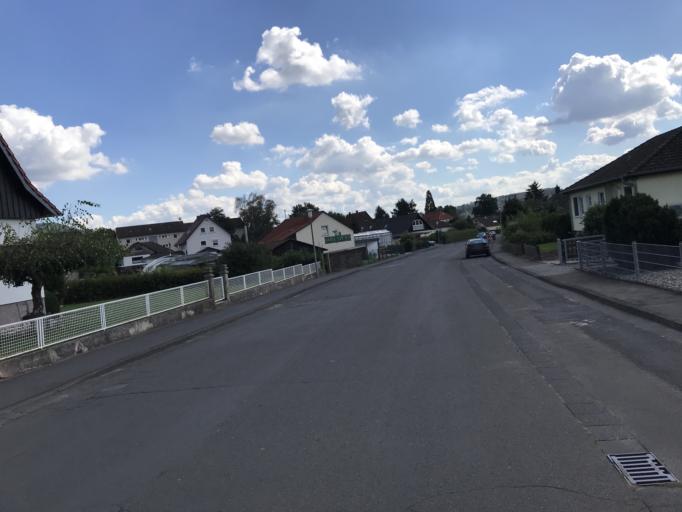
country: DE
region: Hesse
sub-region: Regierungsbezirk Kassel
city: Bad Sooden-Allendorf
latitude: 51.2732
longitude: 9.9796
